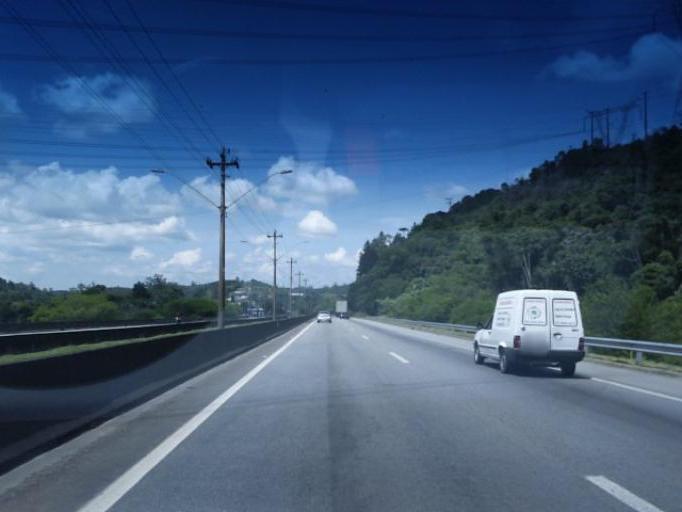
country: BR
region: Sao Paulo
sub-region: Sao Lourenco Da Serra
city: Sao Lourenco da Serra
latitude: -23.8882
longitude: -46.9794
